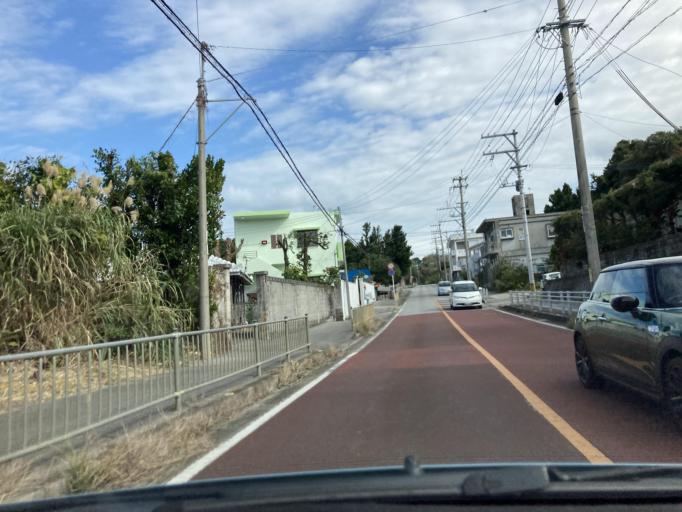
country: JP
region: Okinawa
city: Nago
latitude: 26.6972
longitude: 127.9416
